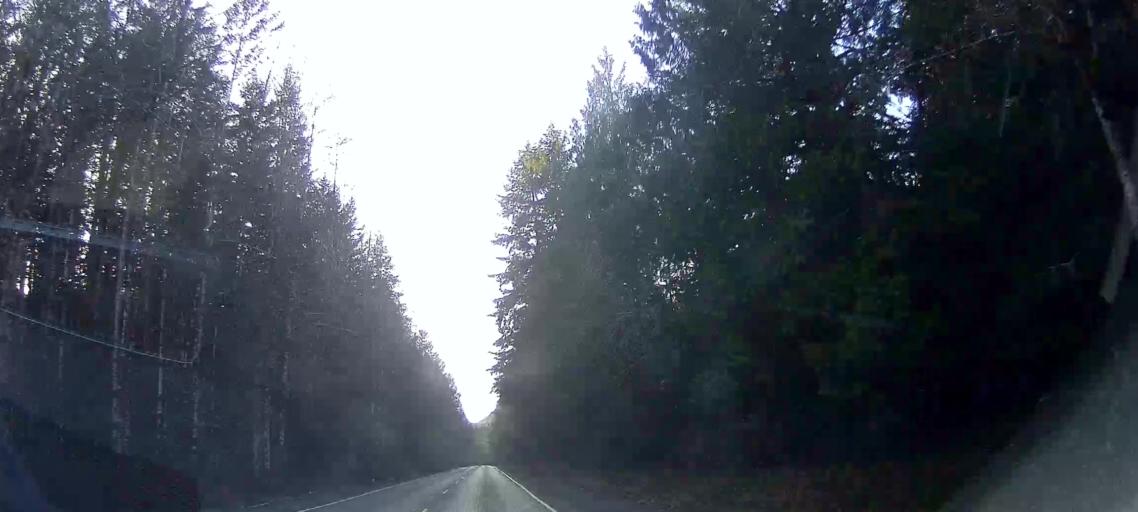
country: US
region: Washington
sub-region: Snohomish County
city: Darrington
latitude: 48.5616
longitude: -121.8224
